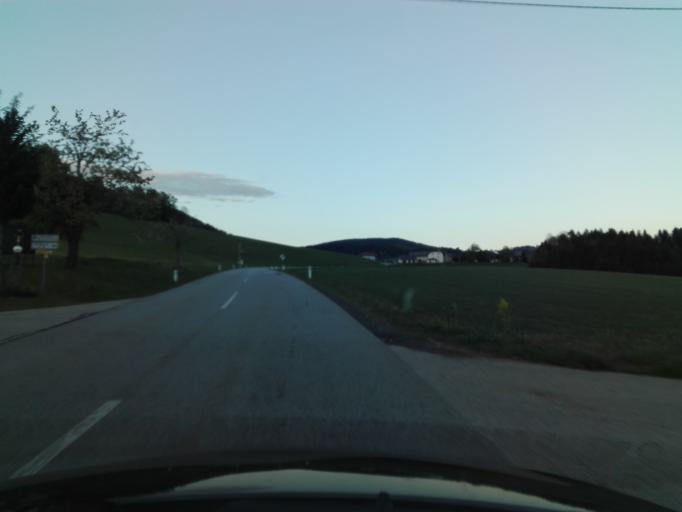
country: DE
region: Bavaria
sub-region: Lower Bavaria
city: Wegscheid
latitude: 48.5477
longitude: 13.7815
